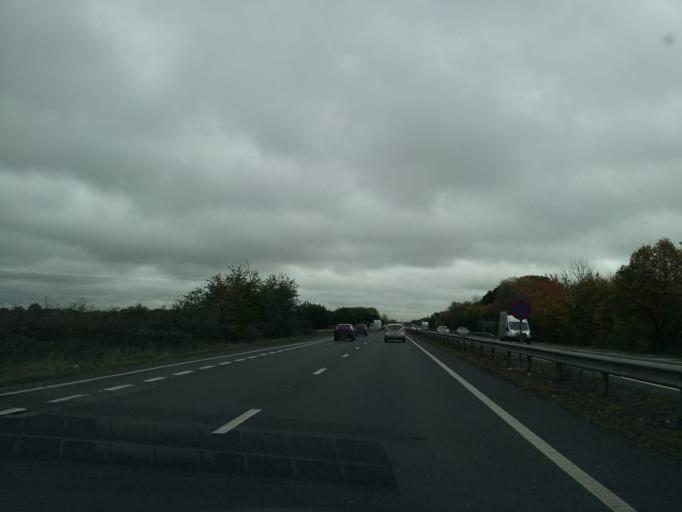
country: GB
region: England
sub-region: Oxfordshire
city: Kidlington
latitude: 51.8303
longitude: -1.2570
